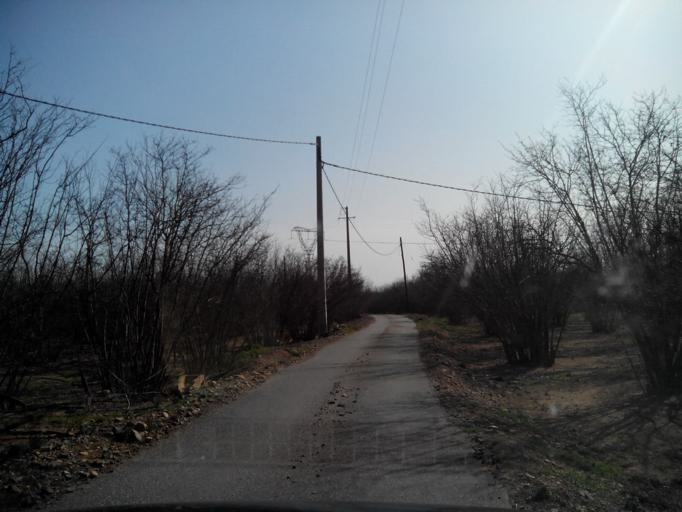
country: ES
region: Catalonia
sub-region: Provincia de Tarragona
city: La Selva
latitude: 41.2130
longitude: 1.1659
